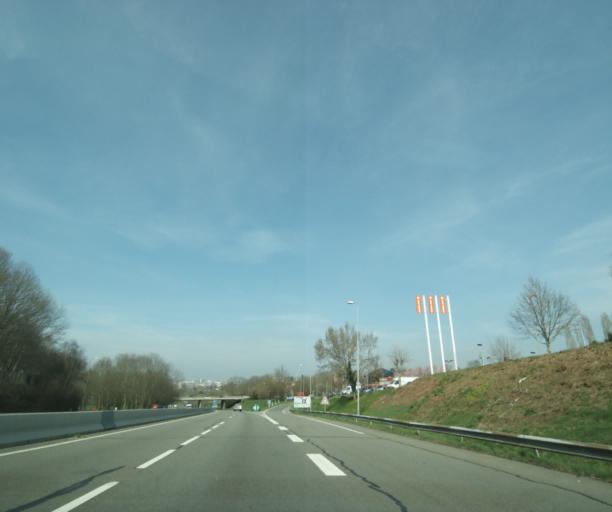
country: FR
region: Limousin
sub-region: Departement de la Haute-Vienne
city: Condat-sur-Vienne
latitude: 45.8165
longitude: 1.2956
